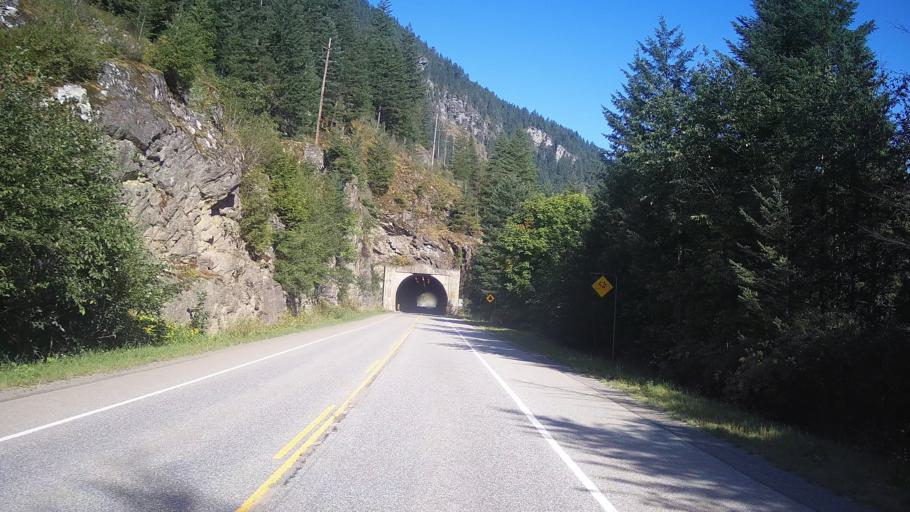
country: CA
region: British Columbia
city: Hope
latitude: 49.6359
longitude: -121.4006
